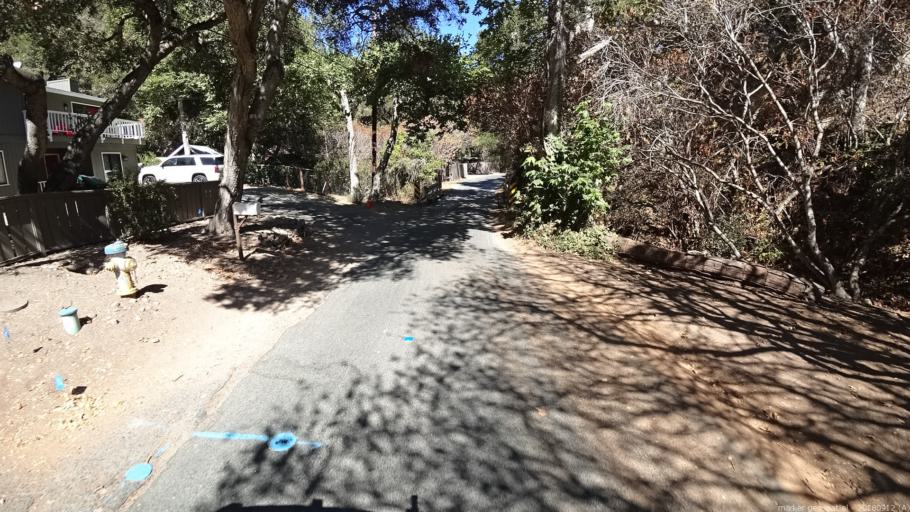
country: US
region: California
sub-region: Monterey County
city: Carmel Valley Village
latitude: 36.4698
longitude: -121.7240
